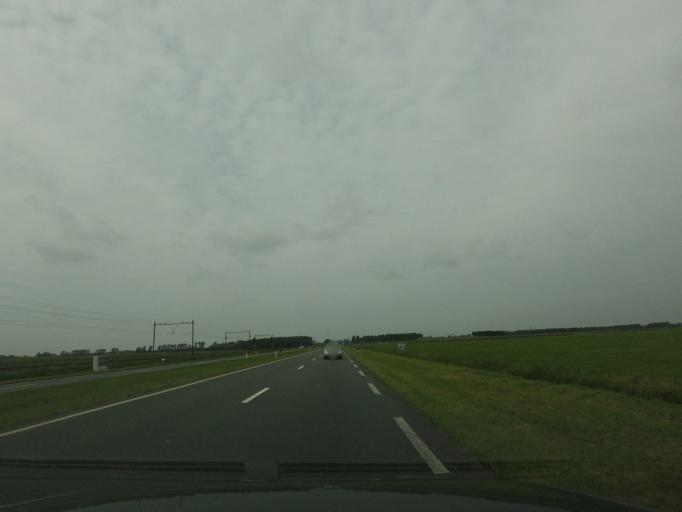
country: NL
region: North Holland
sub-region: Gemeente Uitgeest
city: Uitgeest
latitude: 52.5098
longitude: 4.7255
